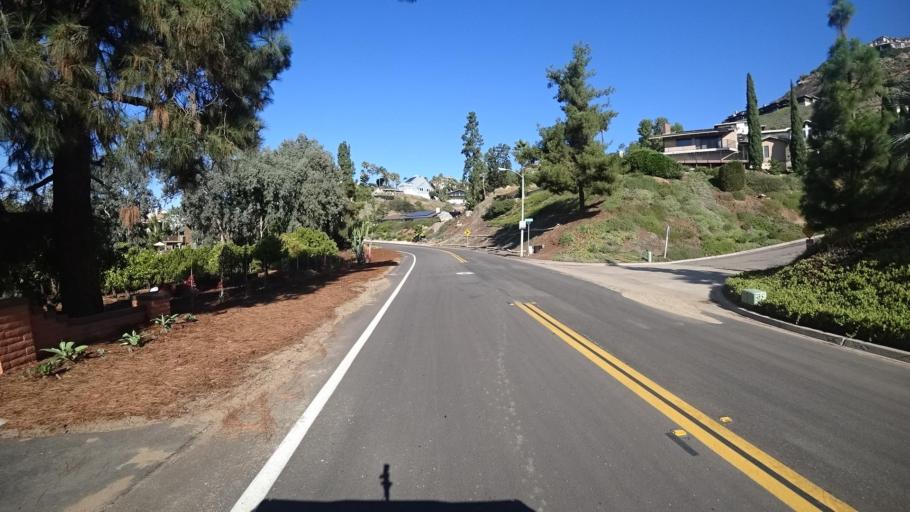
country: US
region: California
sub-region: San Diego County
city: Casa de Oro-Mount Helix
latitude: 32.7631
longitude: -116.9848
